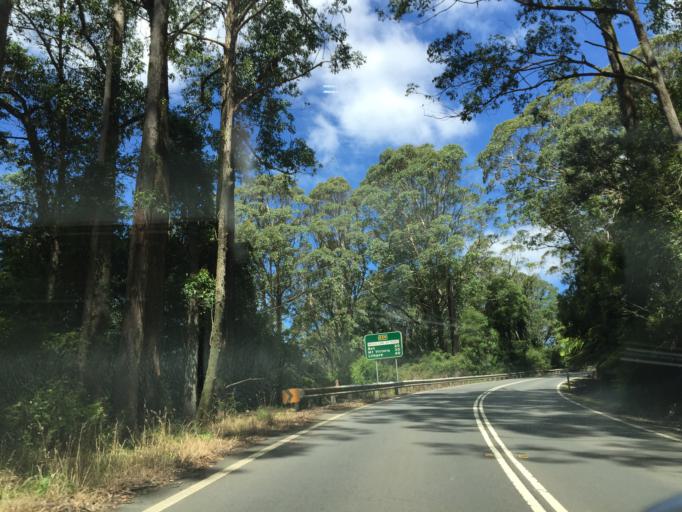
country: AU
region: New South Wales
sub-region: Blue Mountains Municipality
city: Blackheath
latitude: -33.5435
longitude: 150.4258
